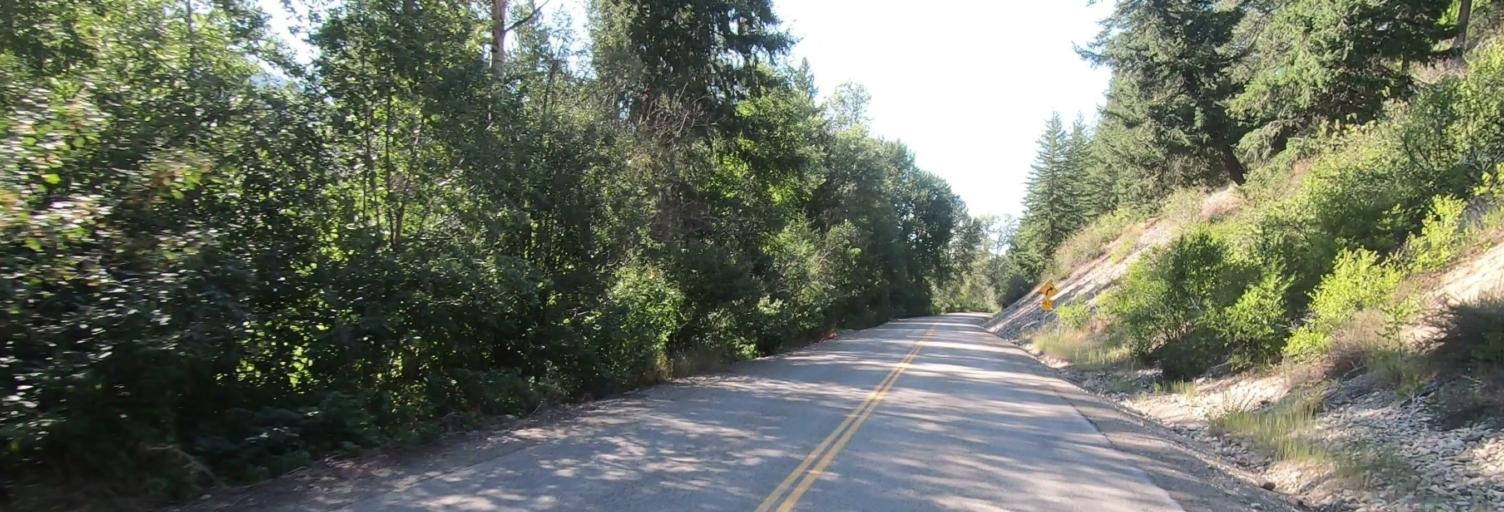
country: US
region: Washington
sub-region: Chelan County
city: Granite Falls
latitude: 48.5540
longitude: -120.3367
